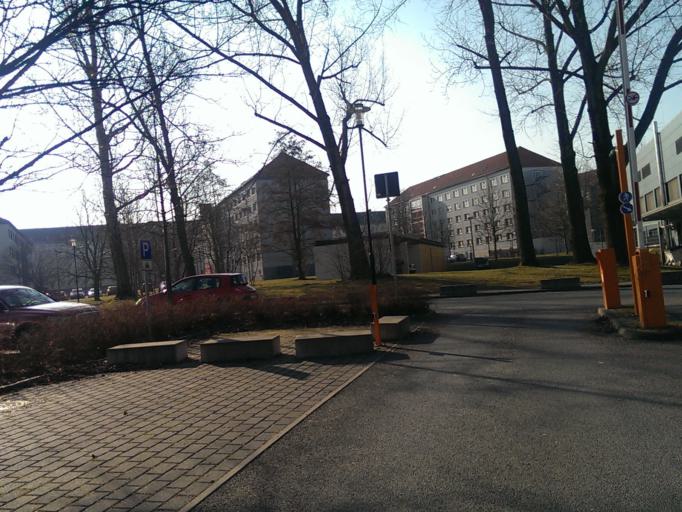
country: DE
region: Saxony
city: Chemnitz
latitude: 50.8160
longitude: 12.9310
